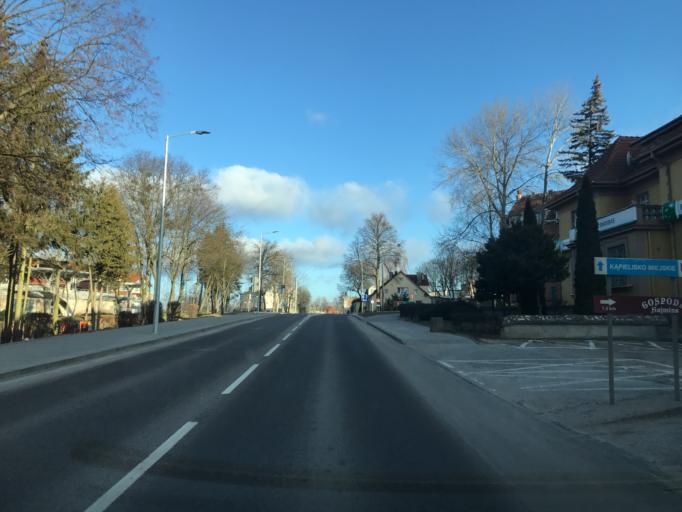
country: PL
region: Warmian-Masurian Voivodeship
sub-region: Powiat ostrodzki
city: Ostroda
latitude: 53.7045
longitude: 19.9600
